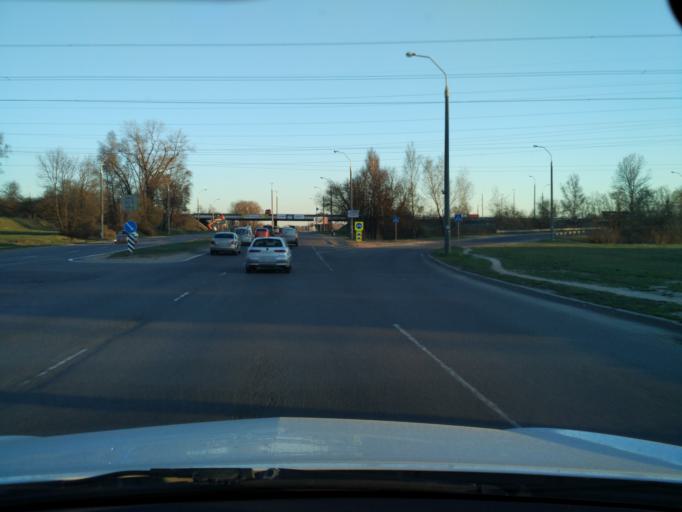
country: BY
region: Minsk
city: Syenitsa
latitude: 53.8380
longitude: 27.5331
